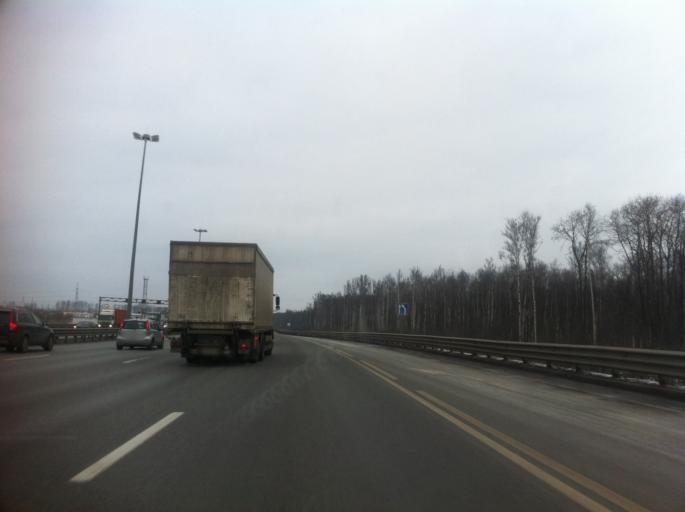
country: RU
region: Leningrad
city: Rybatskoye
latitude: 59.8694
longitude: 30.5316
